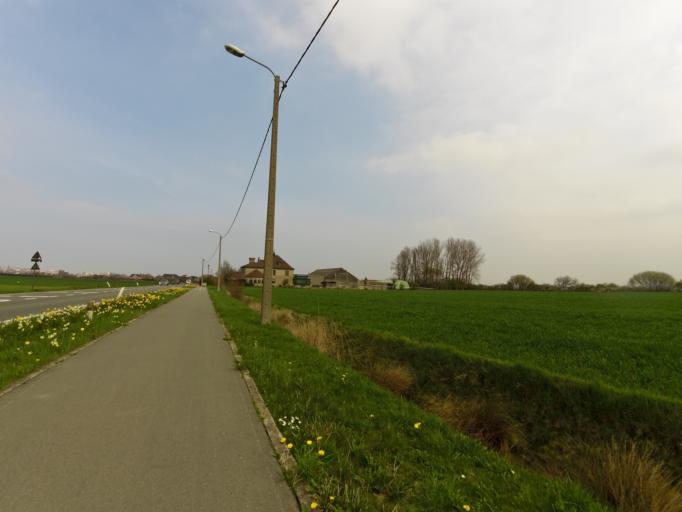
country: BE
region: Flanders
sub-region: Provincie West-Vlaanderen
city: Middelkerke
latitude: 51.1703
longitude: 2.8283
